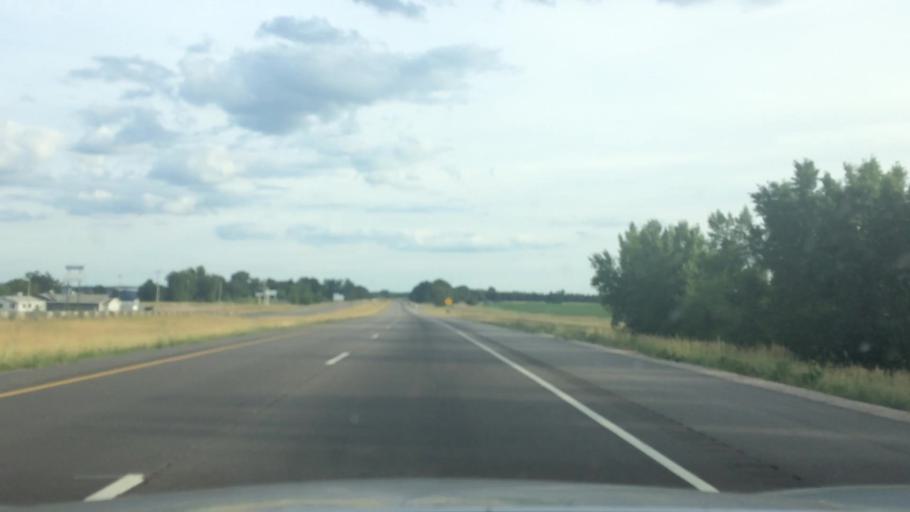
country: US
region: Wisconsin
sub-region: Portage County
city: Plover
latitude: 44.2135
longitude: -89.5248
